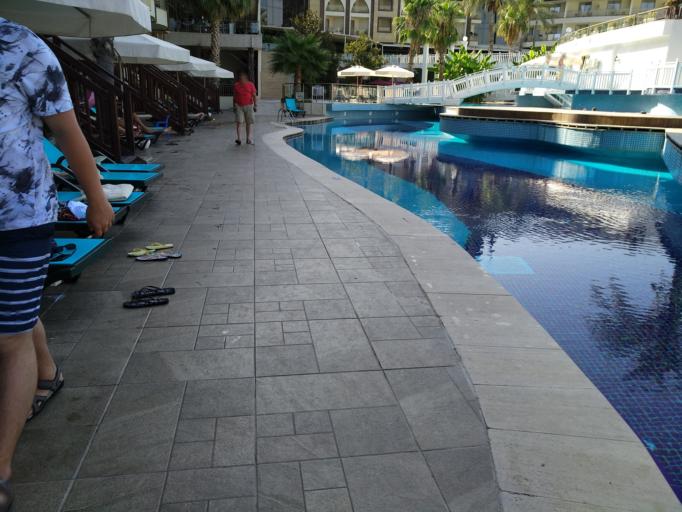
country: TR
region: Antalya
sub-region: Kemer
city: Goeynuek
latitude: 36.6649
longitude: 30.5596
